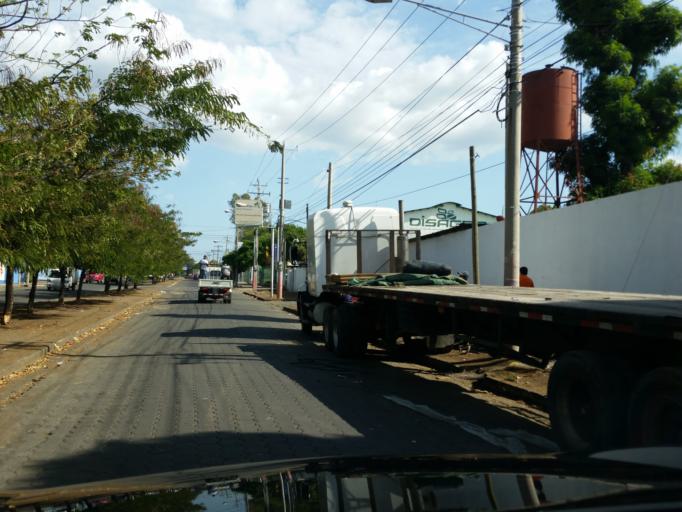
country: NI
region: Managua
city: Managua
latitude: 12.1548
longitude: -86.2240
